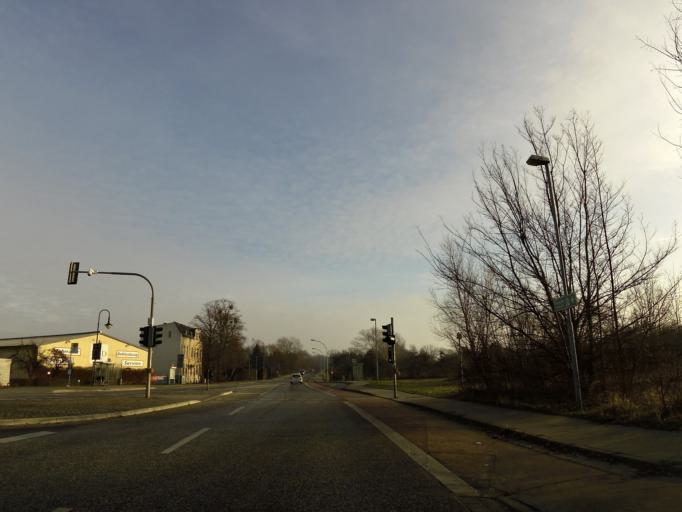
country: DE
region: Brandenburg
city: Werder
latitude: 52.3641
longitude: 12.9409
